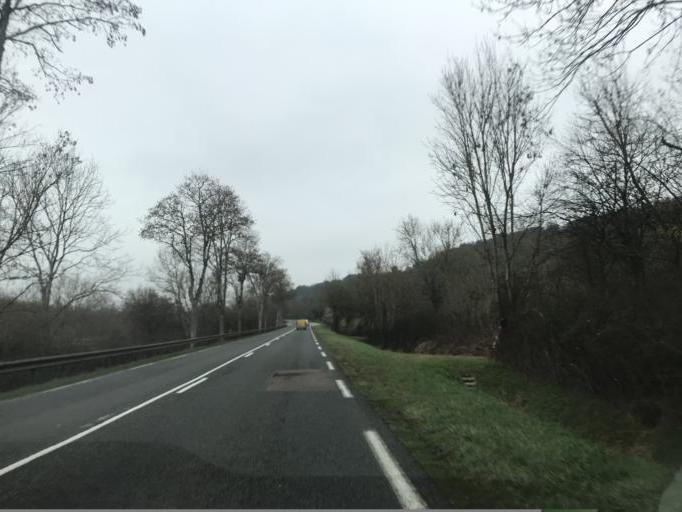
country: FR
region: Bourgogne
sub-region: Departement de l'Yonne
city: Avallon
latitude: 47.5178
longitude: 3.8117
